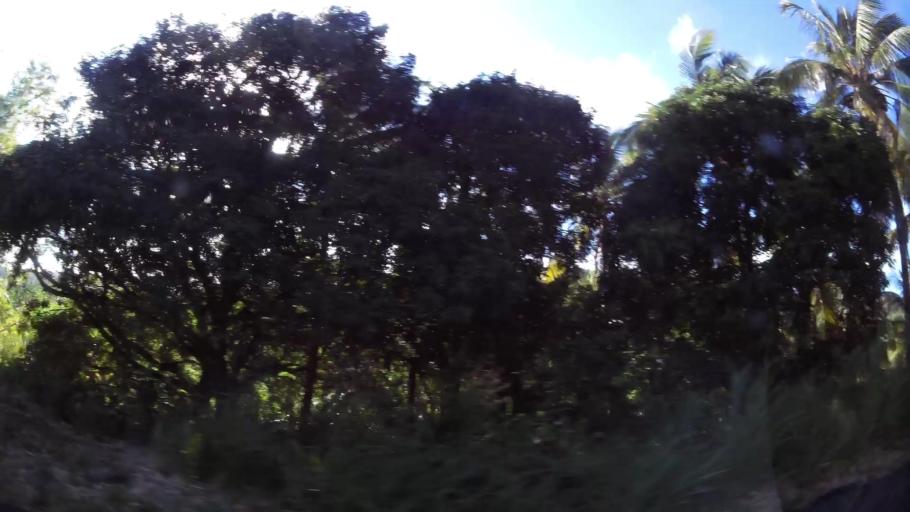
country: DM
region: Saint John
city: Portsmouth
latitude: 15.5790
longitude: -61.4179
